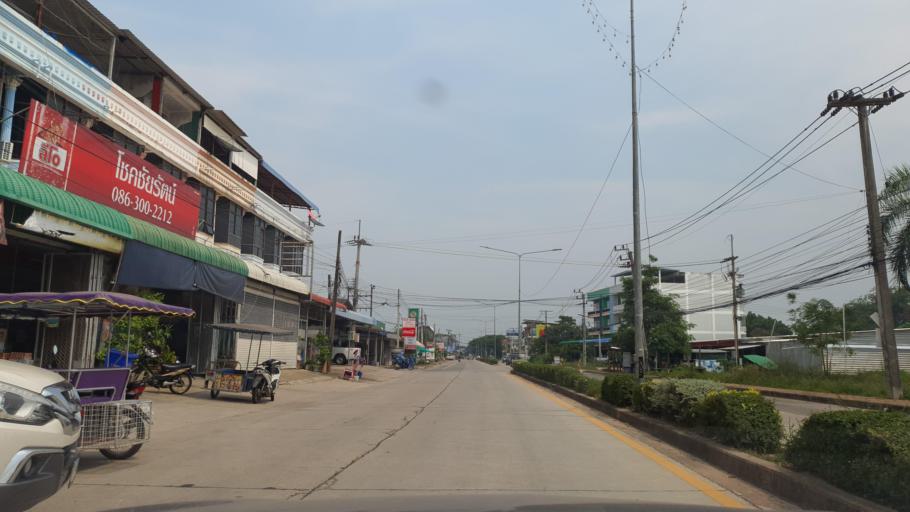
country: TH
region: Rayong
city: Rayong
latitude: 12.6261
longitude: 101.4239
